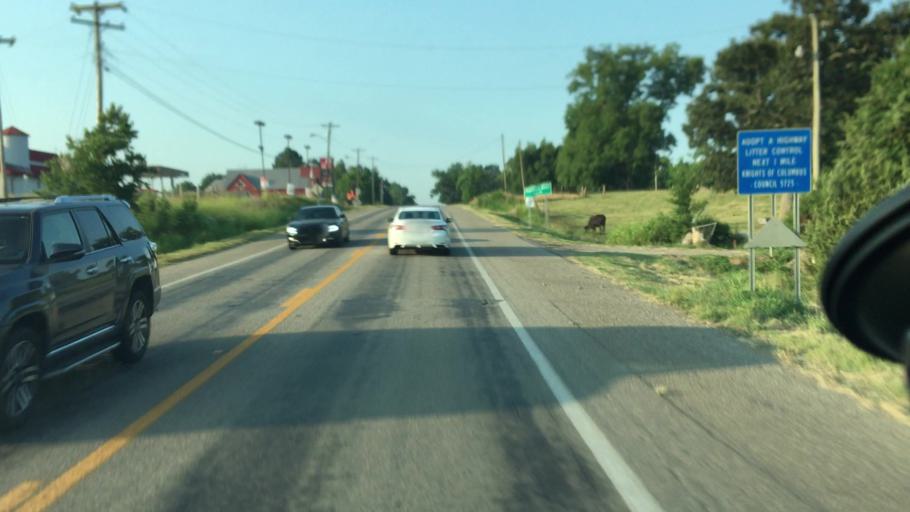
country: US
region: Arkansas
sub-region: Johnson County
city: Clarksville
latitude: 35.3895
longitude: -93.5301
